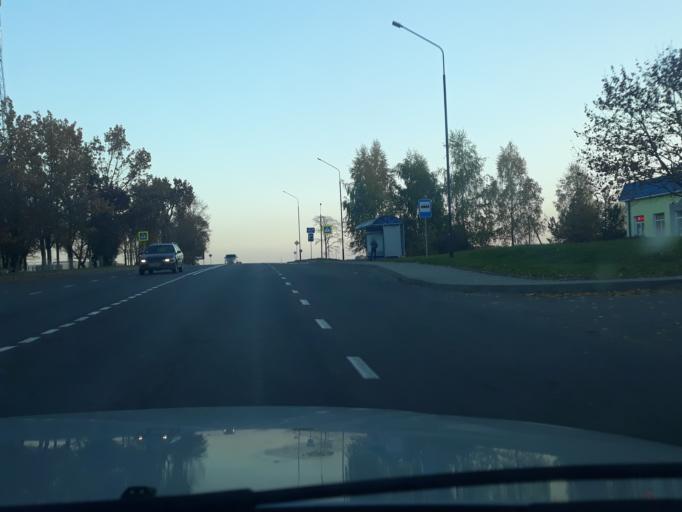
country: BY
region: Grodnenskaya
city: Vawkavysk
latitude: 53.1489
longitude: 24.4610
